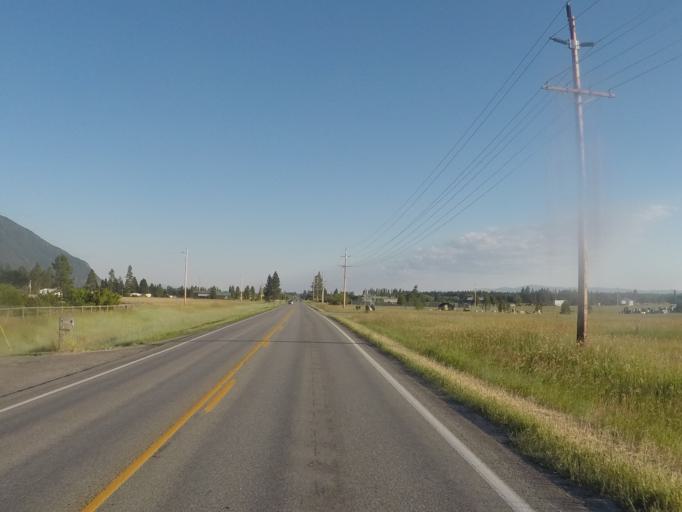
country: US
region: Montana
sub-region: Flathead County
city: Columbia Falls
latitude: 48.3534
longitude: -114.1593
